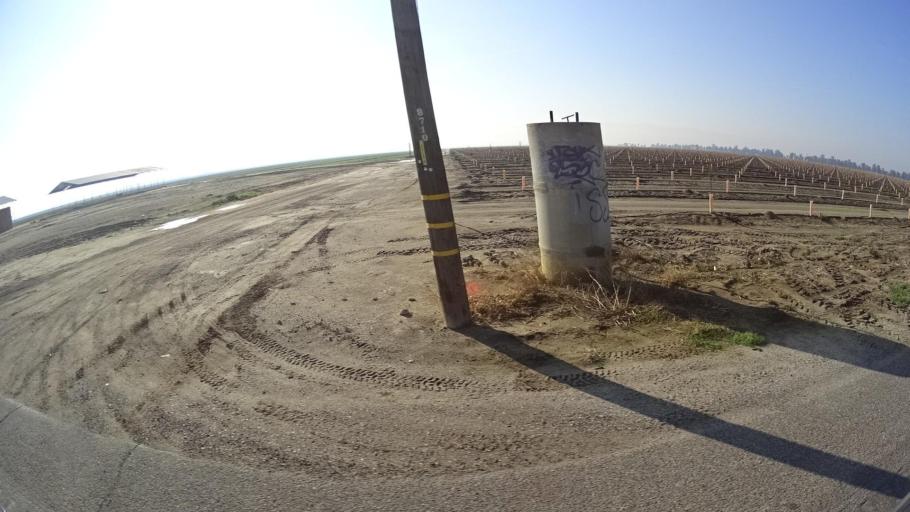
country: US
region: California
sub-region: Kern County
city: Greenfield
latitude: 35.2086
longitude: -118.9855
